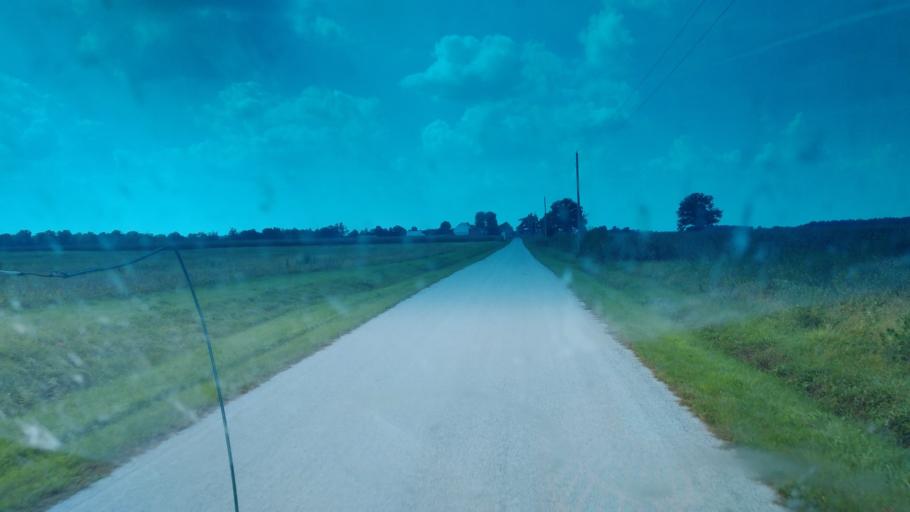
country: US
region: Ohio
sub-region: Hardin County
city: Kenton
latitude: 40.6893
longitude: -83.7145
